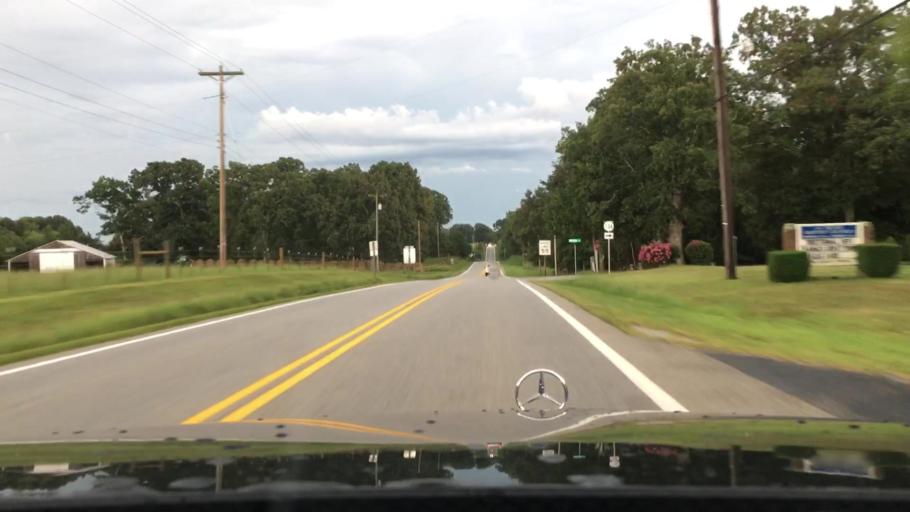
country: US
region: Virginia
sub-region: Amherst County
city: Amherst
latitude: 37.6353
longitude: -79.0215
